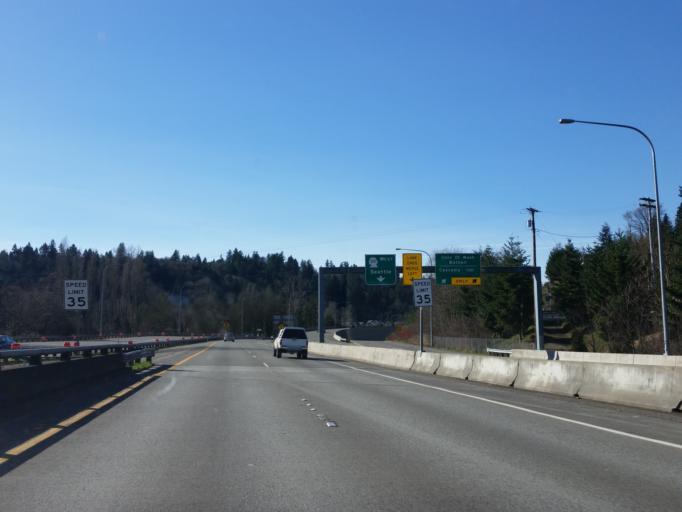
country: US
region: Washington
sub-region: King County
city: Bothell
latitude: 47.7572
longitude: -122.1888
